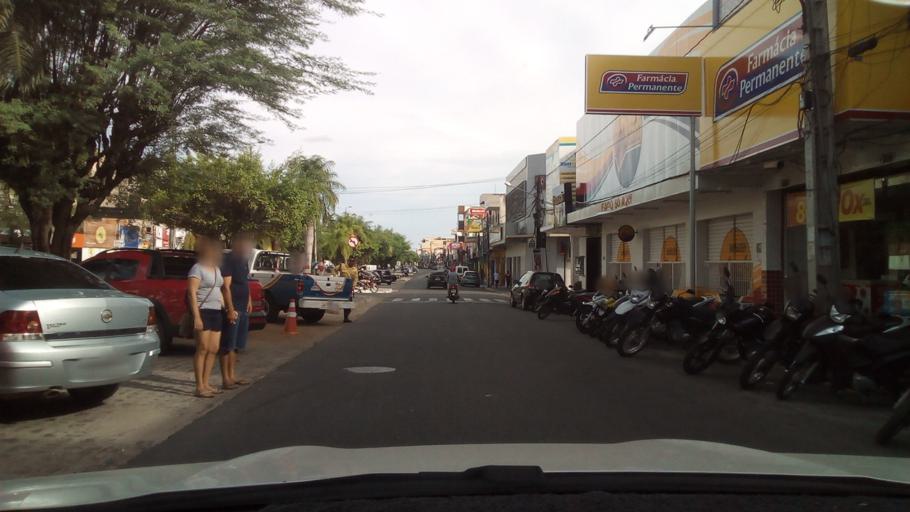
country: BR
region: Paraiba
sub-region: Guarabira
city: Guarabira
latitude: -6.8518
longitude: -35.4920
